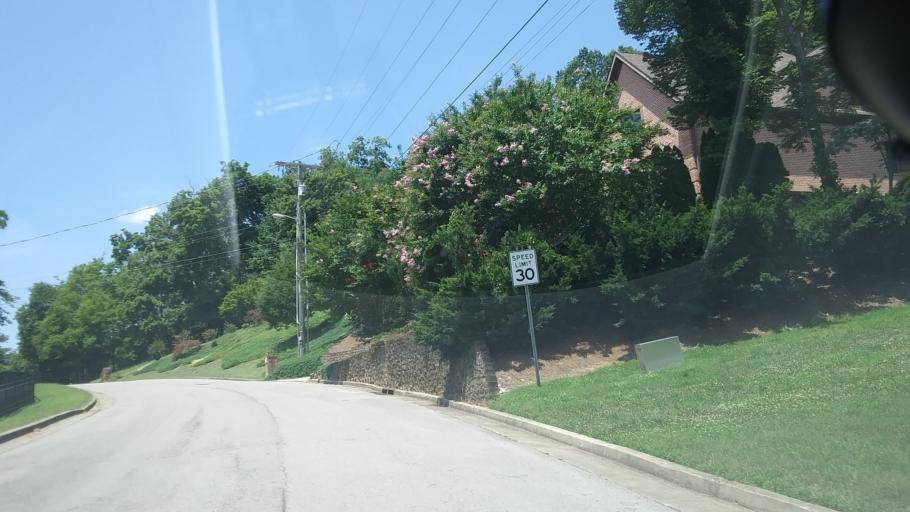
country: US
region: Tennessee
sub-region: Davidson County
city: Belle Meade
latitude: 36.0903
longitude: -86.9454
